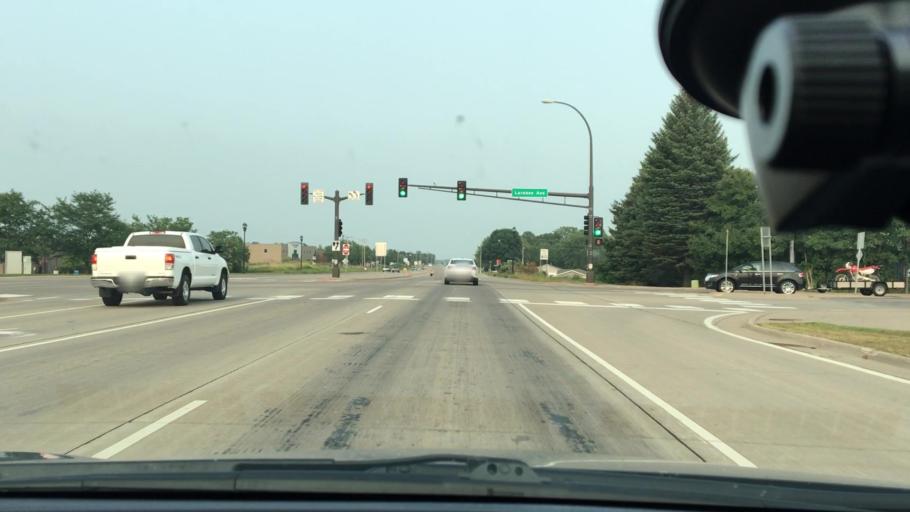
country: US
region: Minnesota
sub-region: Wright County
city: Saint Michael
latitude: 45.2102
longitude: -93.6477
